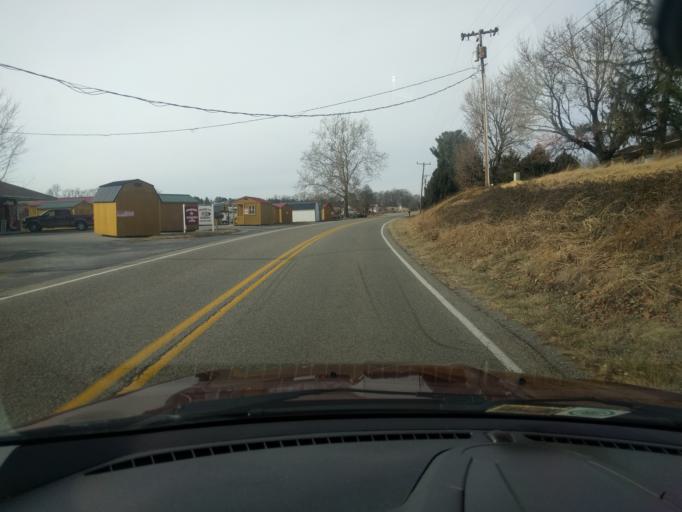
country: US
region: Virginia
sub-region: Augusta County
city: Stuarts Draft
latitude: 38.0312
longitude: -79.0607
